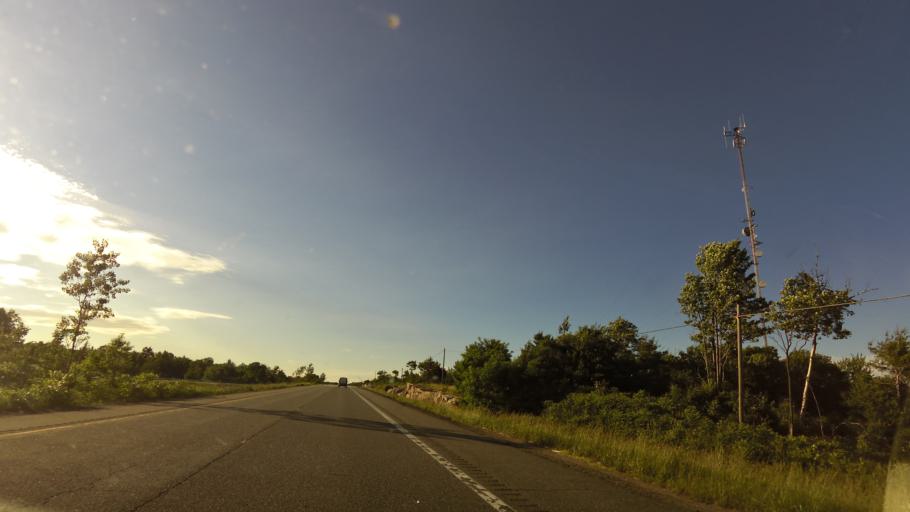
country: CA
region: Ontario
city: Midland
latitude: 44.8512
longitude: -79.7372
